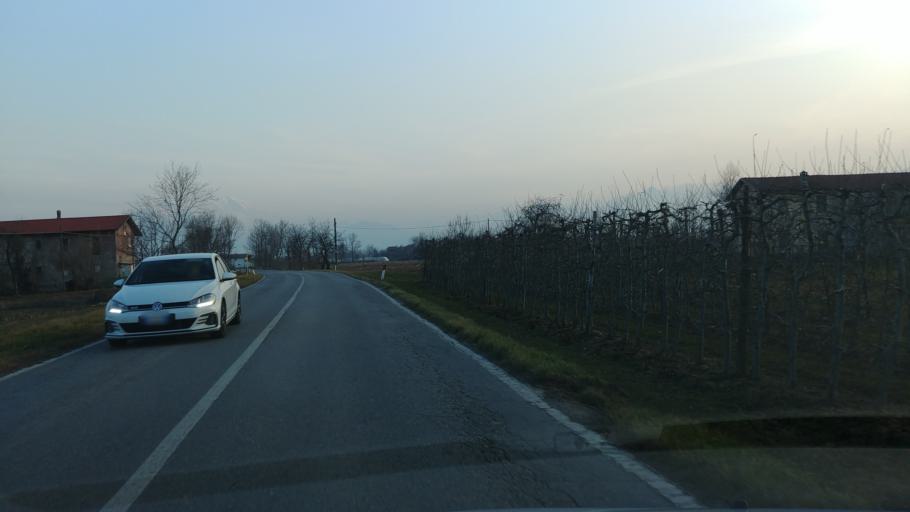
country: IT
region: Piedmont
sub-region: Provincia di Cuneo
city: Roata Rossi
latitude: 44.4212
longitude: 7.5077
